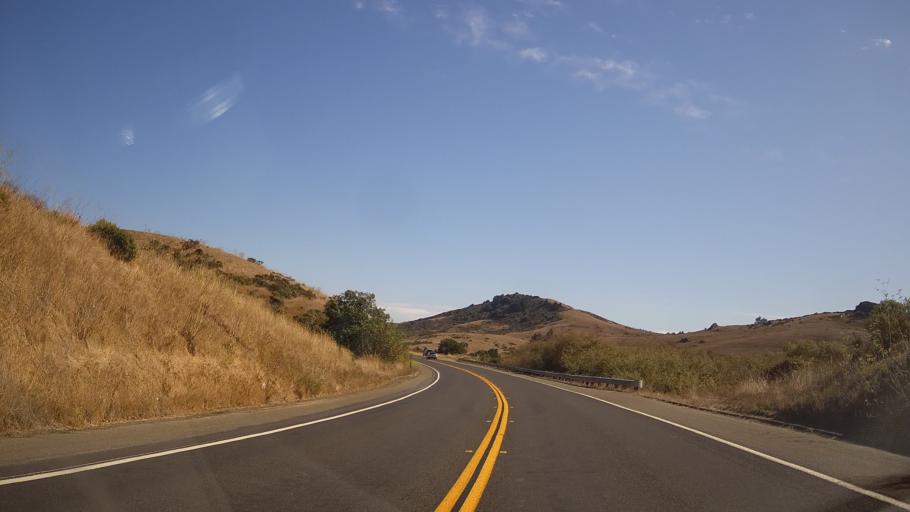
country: US
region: California
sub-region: Marin County
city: Lagunitas-Forest Knolls
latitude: 38.0910
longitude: -122.7307
